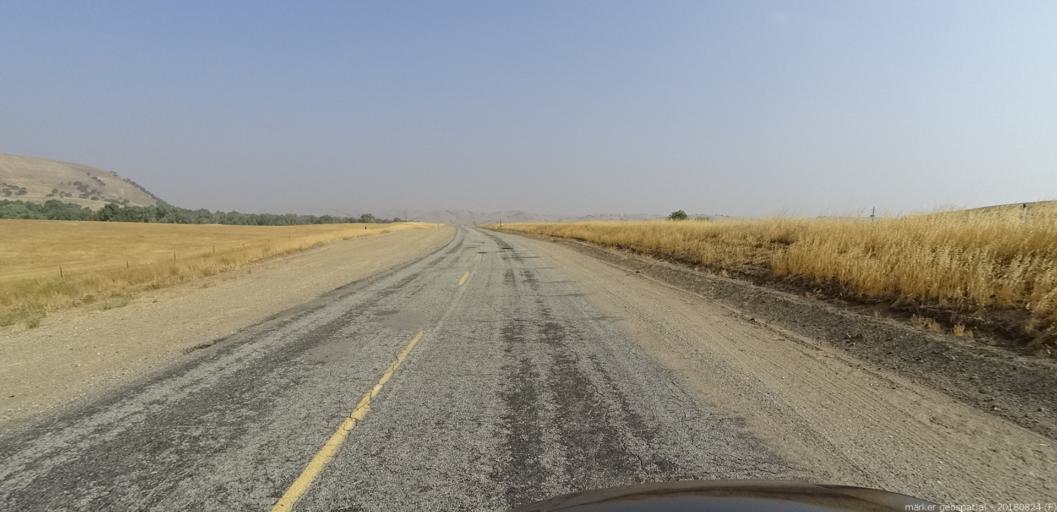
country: US
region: California
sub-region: San Luis Obispo County
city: San Miguel
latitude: 35.8303
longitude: -120.7502
